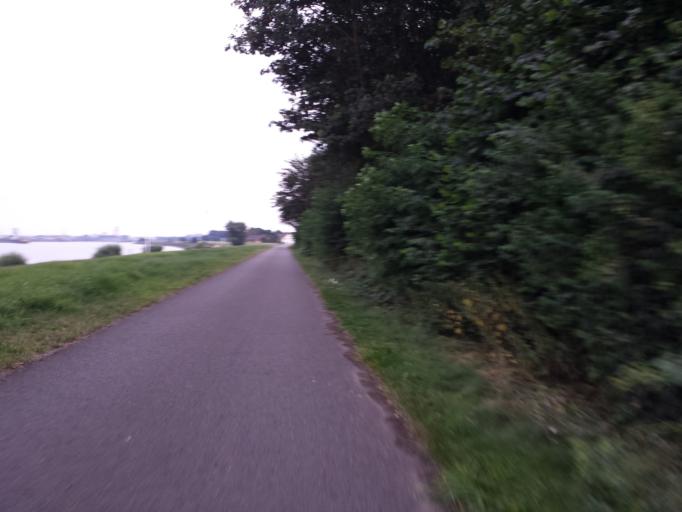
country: DE
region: Lower Saxony
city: Ritterhude
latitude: 53.1196
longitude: 8.6855
